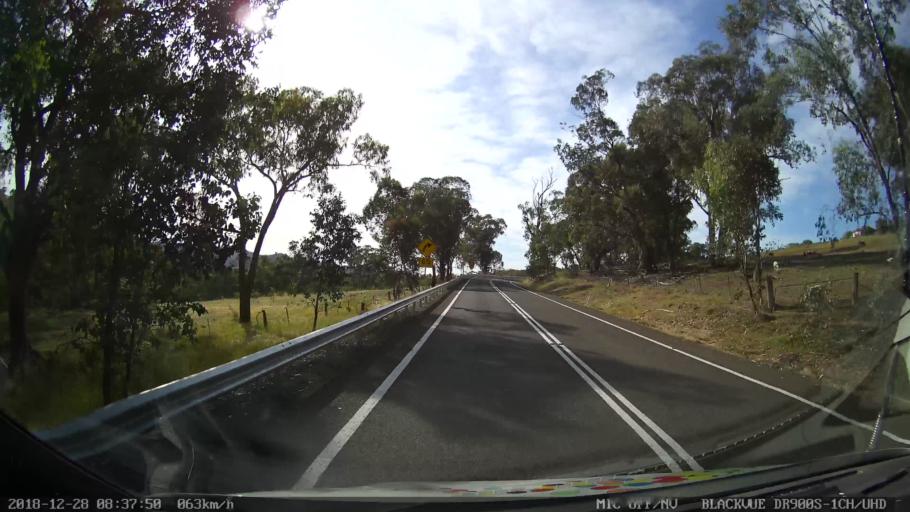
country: AU
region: New South Wales
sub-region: Blayney
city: Blayney
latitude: -33.9986
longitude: 149.3137
